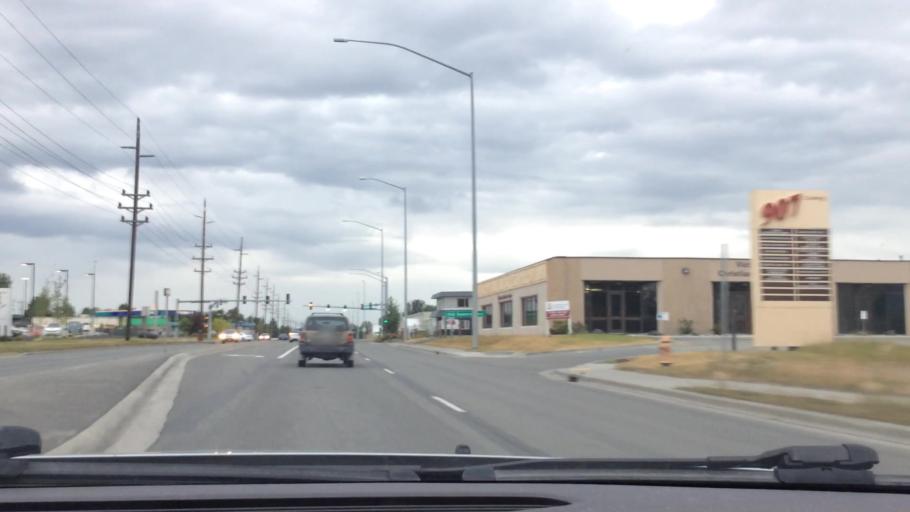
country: US
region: Alaska
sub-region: Anchorage Municipality
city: Anchorage
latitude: 61.1664
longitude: -149.8647
